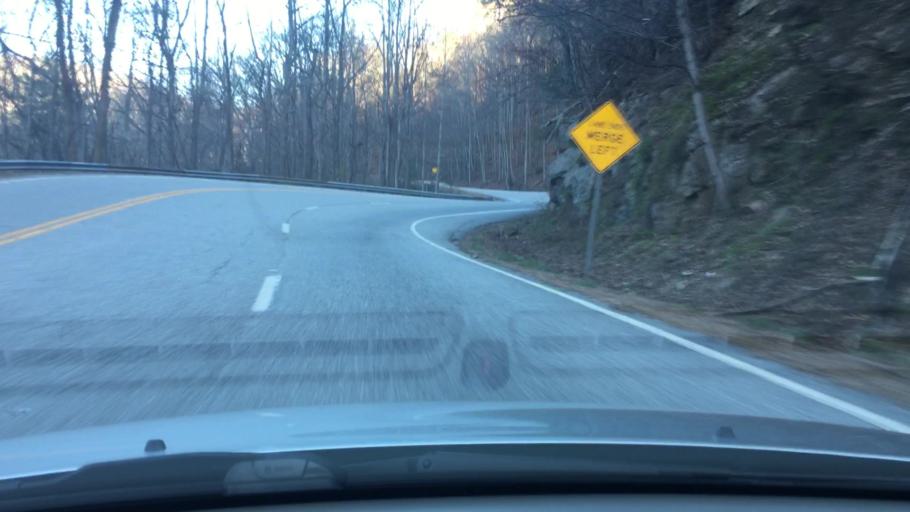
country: US
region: Georgia
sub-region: Union County
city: Blairsville
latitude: 34.7193
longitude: -83.9078
